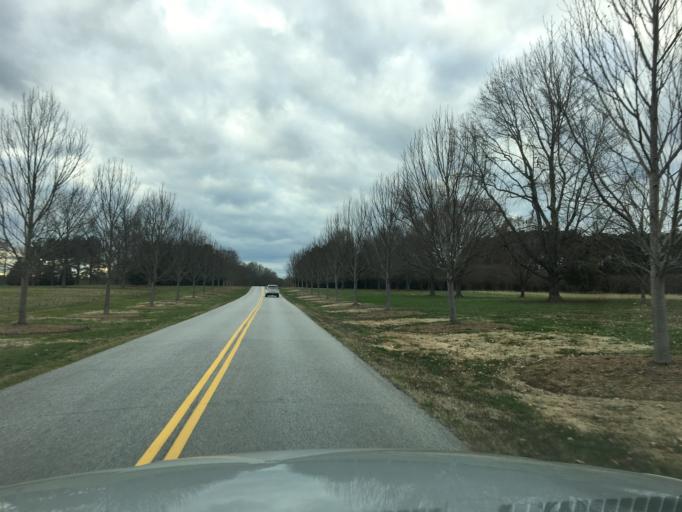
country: US
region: South Carolina
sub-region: Spartanburg County
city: Saxon
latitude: 34.9874
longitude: -81.9495
